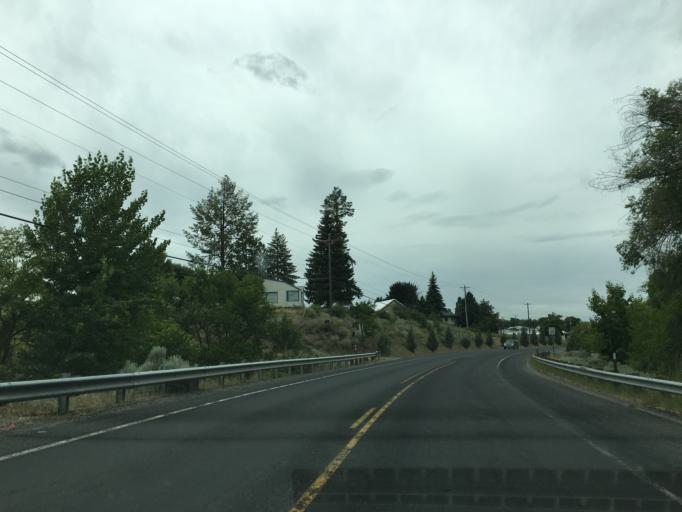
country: US
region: Washington
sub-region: Okanogan County
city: Coulee Dam
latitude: 47.9344
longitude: -119.0283
